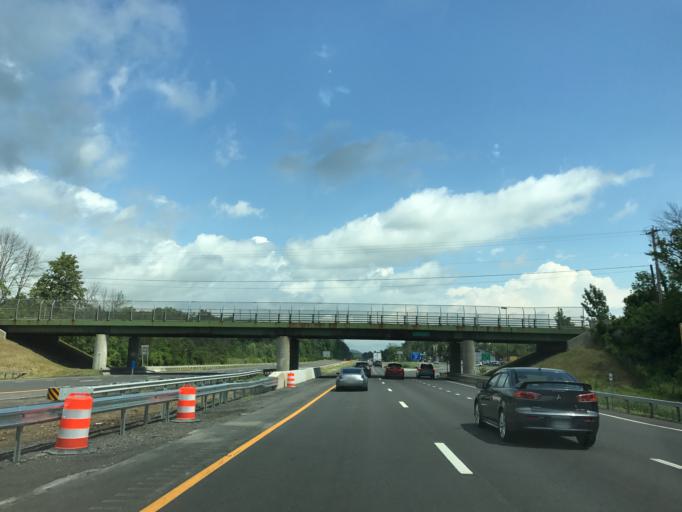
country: US
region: New York
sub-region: Ulster County
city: Saugerties
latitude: 42.1074
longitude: -73.9580
